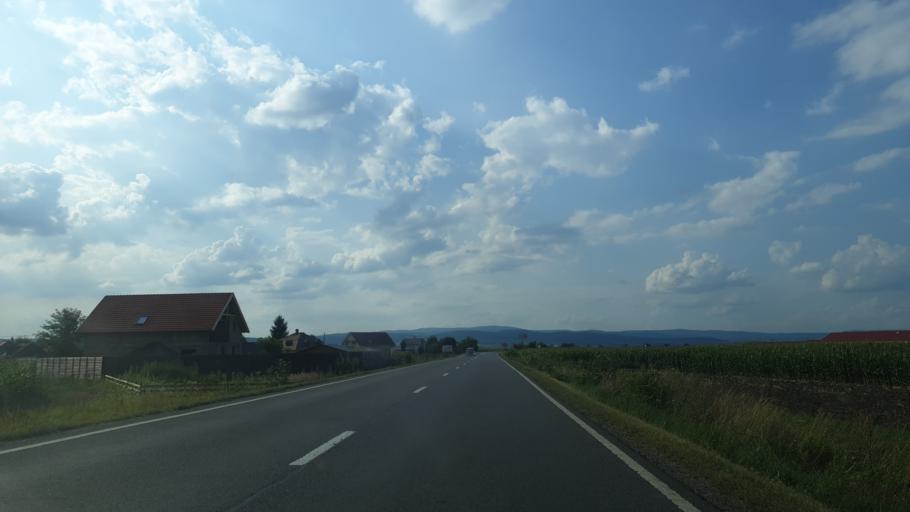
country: RO
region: Covasna
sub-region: Comuna Chichis
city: Chichis
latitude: 45.7788
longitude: 25.8082
